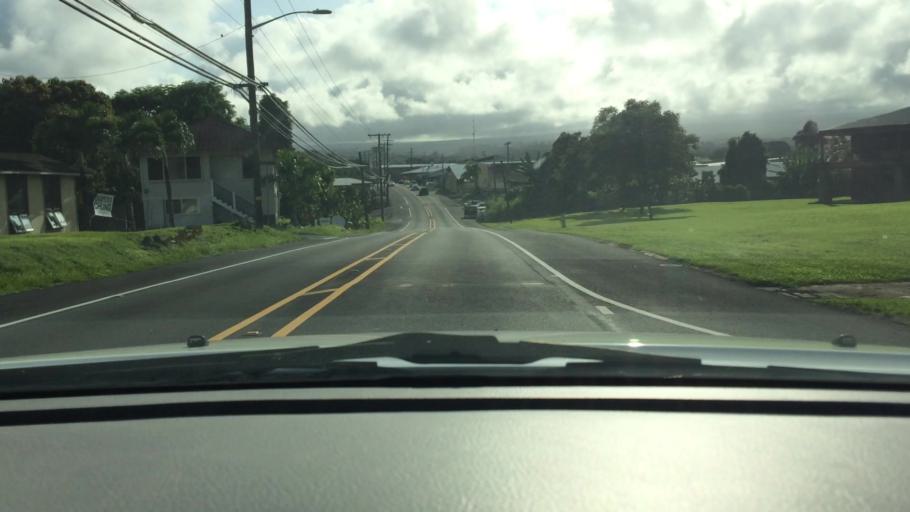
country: US
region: Hawaii
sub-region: Hawaii County
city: Hilo
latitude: 19.7118
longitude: -155.0733
